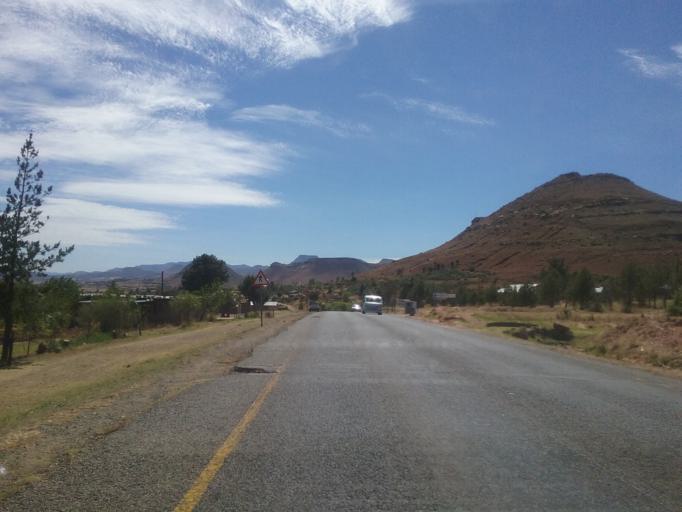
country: LS
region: Mohale's Hoek District
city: Mohale's Hoek
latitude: -30.1872
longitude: 27.4195
